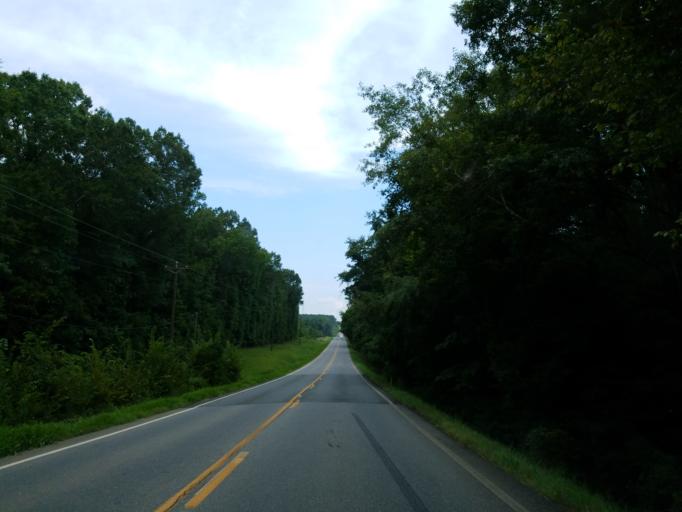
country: US
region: Georgia
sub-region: Dooly County
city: Unadilla
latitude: 32.3278
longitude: -83.7352
